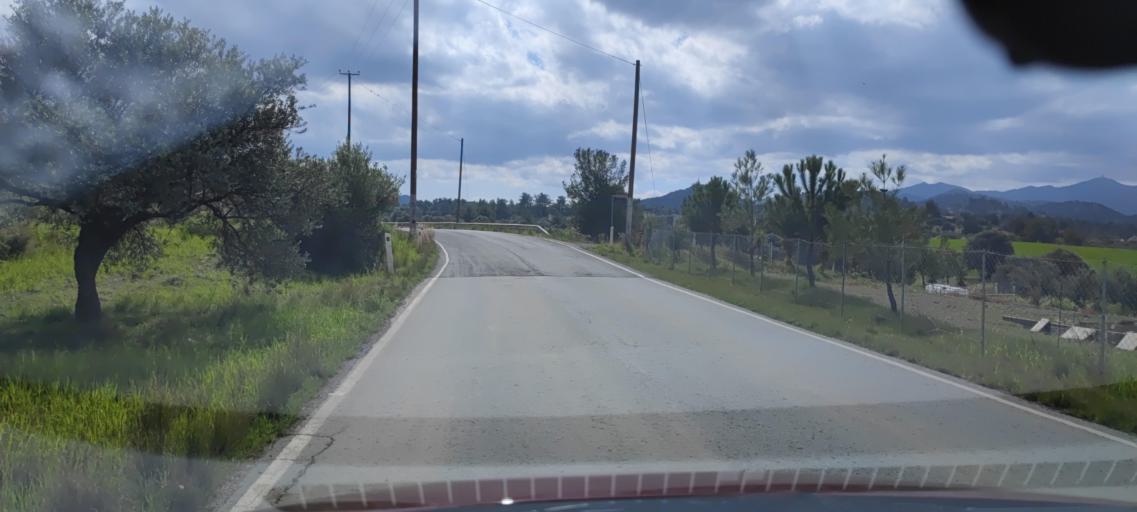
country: CY
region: Lefkosia
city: Lythrodontas
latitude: 34.9873
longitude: 33.2964
